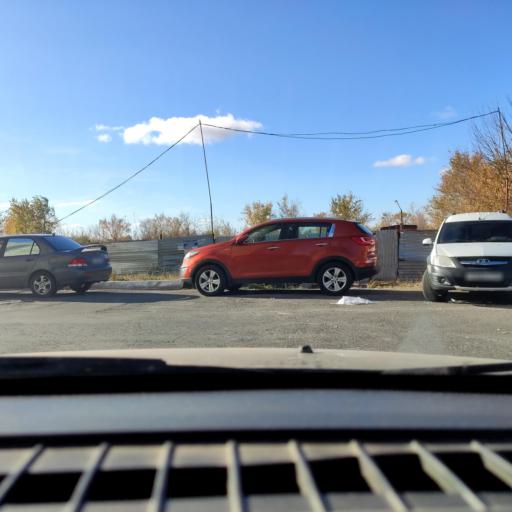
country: RU
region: Samara
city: Tol'yatti
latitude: 53.5137
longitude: 49.2552
